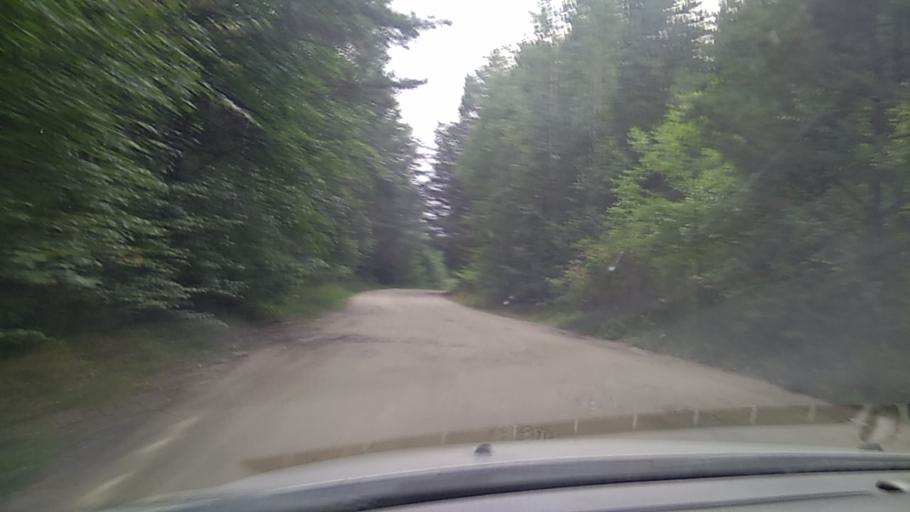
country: RU
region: Chelyabinsk
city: Kyshtym
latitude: 55.6791
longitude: 60.5810
